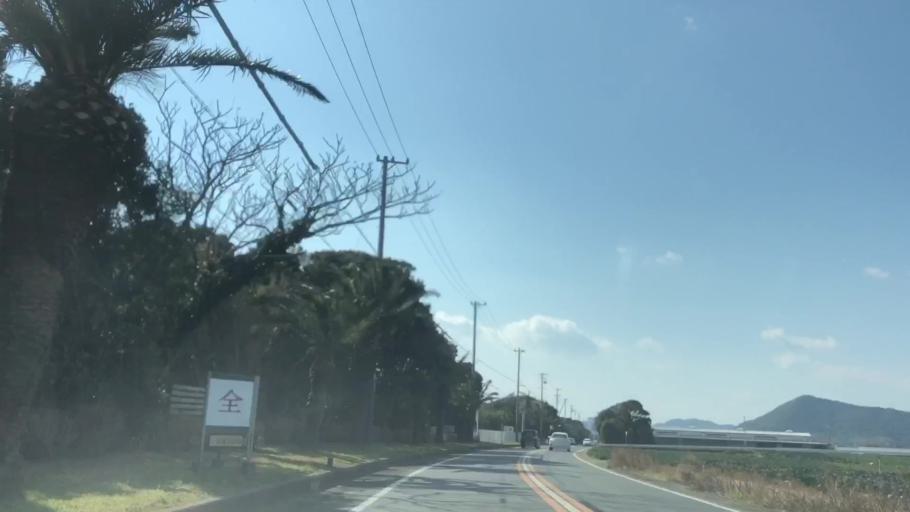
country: JP
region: Aichi
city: Toyohama
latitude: 34.5907
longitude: 137.0878
